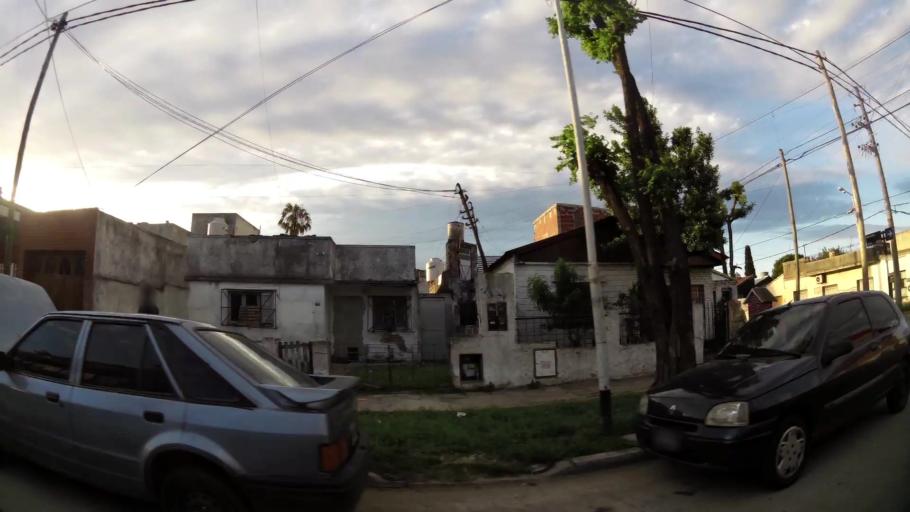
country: AR
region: Buenos Aires
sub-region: Partido de Avellaneda
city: Avellaneda
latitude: -34.7007
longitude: -58.3379
